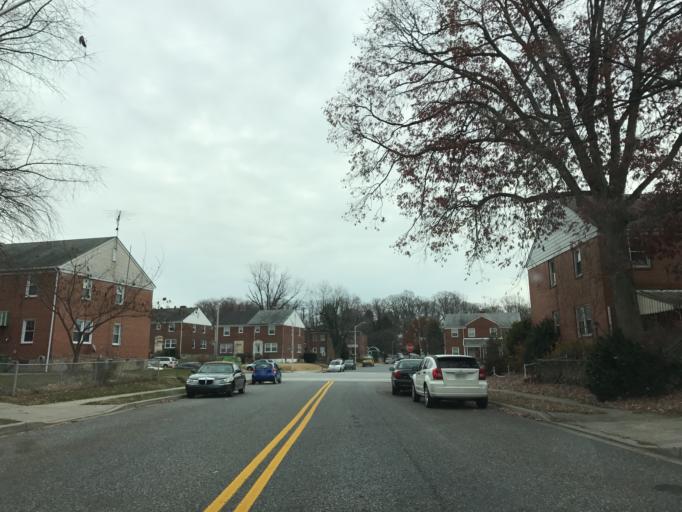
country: US
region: Maryland
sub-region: Baltimore County
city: Parkville
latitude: 39.3508
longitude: -76.5462
